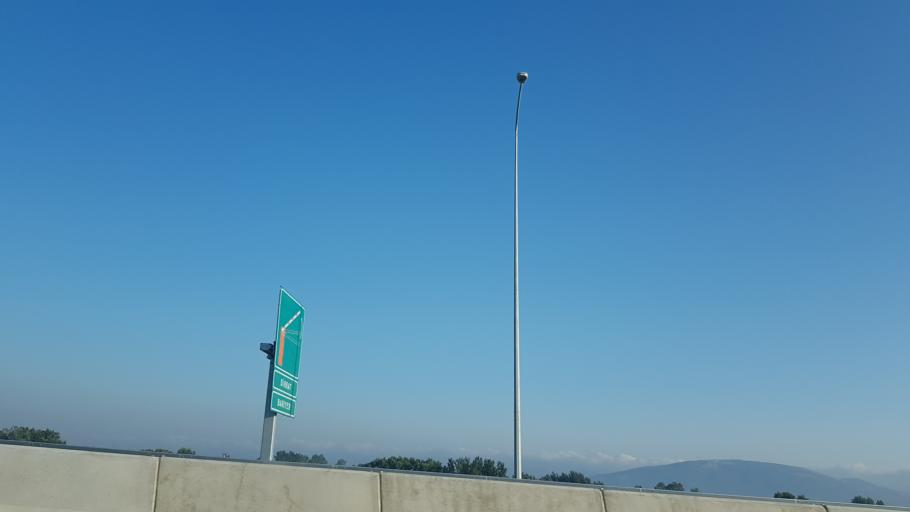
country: TR
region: Bursa
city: Karacabey
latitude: 40.1911
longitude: 28.3445
